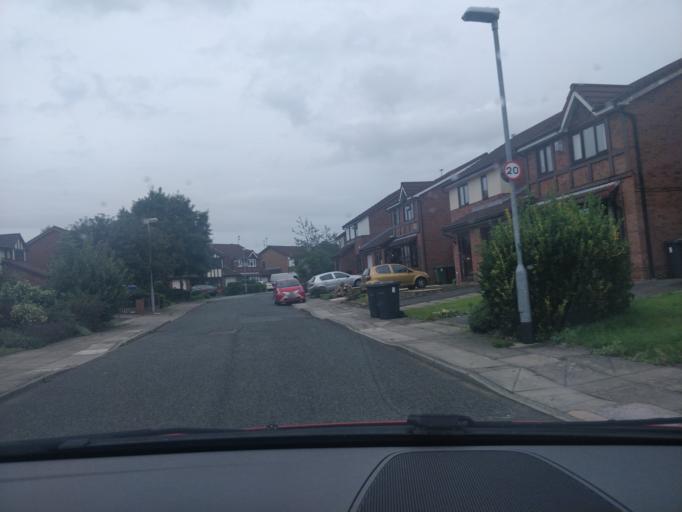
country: GB
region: England
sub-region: Sefton
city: Southport
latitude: 53.6351
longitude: -2.9833
